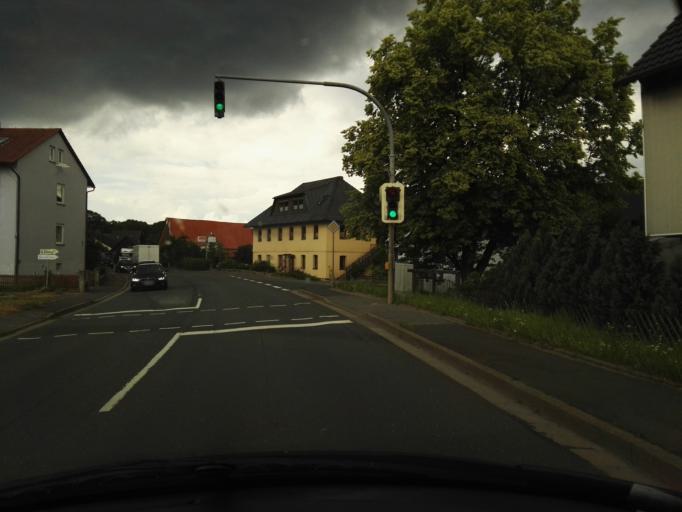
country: DE
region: Bavaria
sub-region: Upper Franconia
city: Michelau
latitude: 50.1471
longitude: 11.1393
